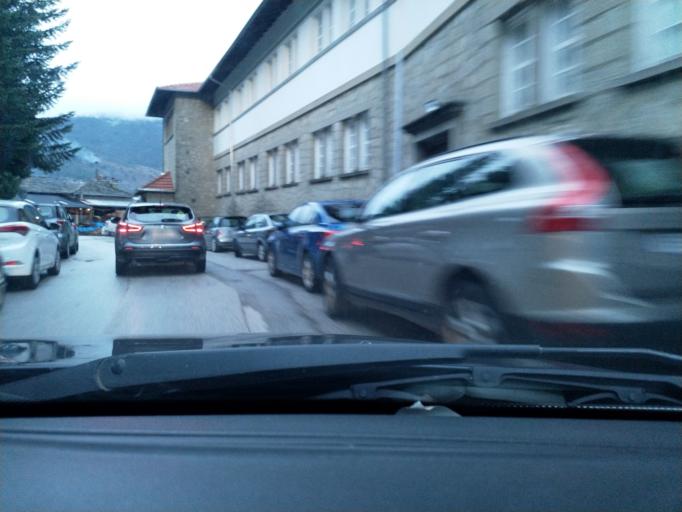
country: GR
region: Epirus
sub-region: Nomos Ioanninon
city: Metsovo
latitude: 39.7692
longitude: 21.1840
